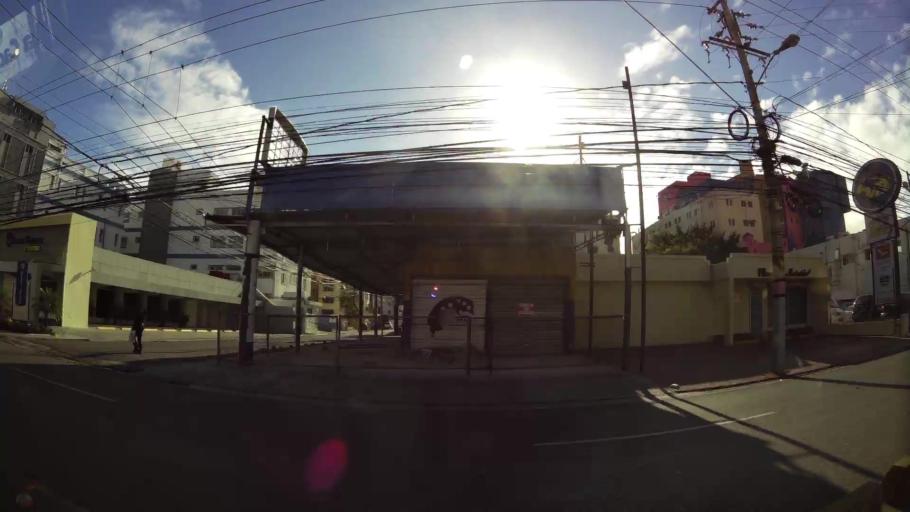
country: DO
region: Nacional
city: La Julia
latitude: 18.4707
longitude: -69.9316
